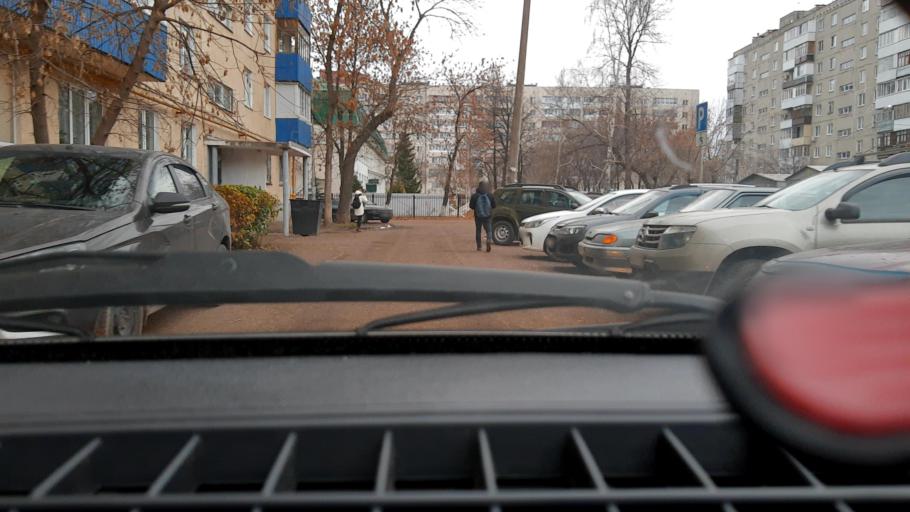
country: RU
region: Bashkortostan
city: Ufa
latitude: 54.7776
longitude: 56.1293
